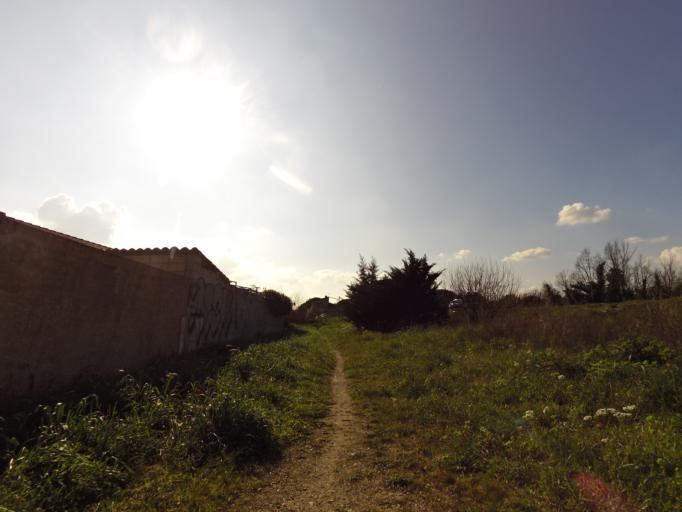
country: FR
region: Languedoc-Roussillon
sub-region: Departement du Gard
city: Codognan
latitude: 43.7289
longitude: 4.2252
